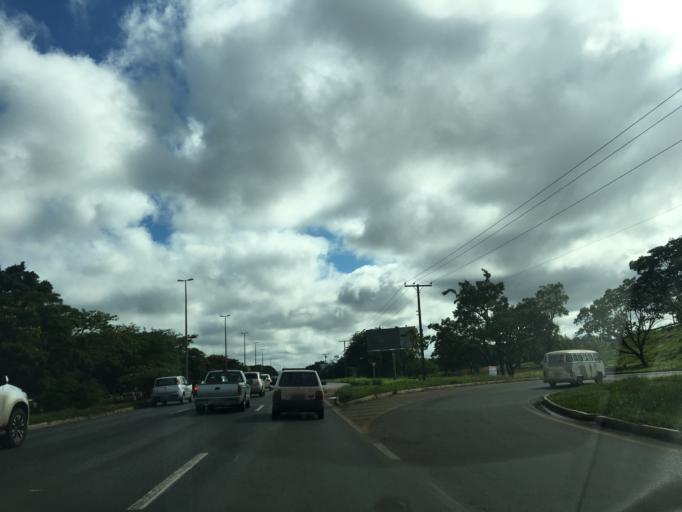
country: BR
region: Federal District
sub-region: Brasilia
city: Brasilia
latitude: -15.8699
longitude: -47.9486
